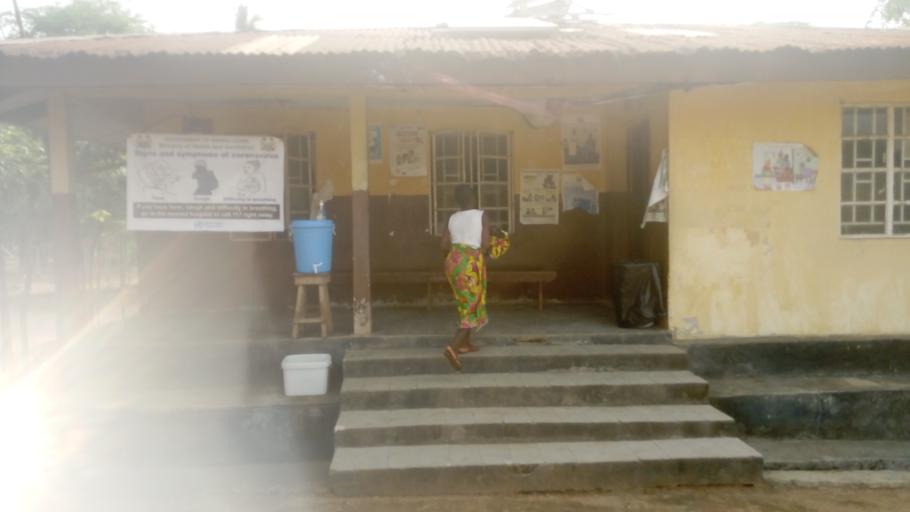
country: SL
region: Northern Province
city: Makeni
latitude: 8.8625
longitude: -12.0558
